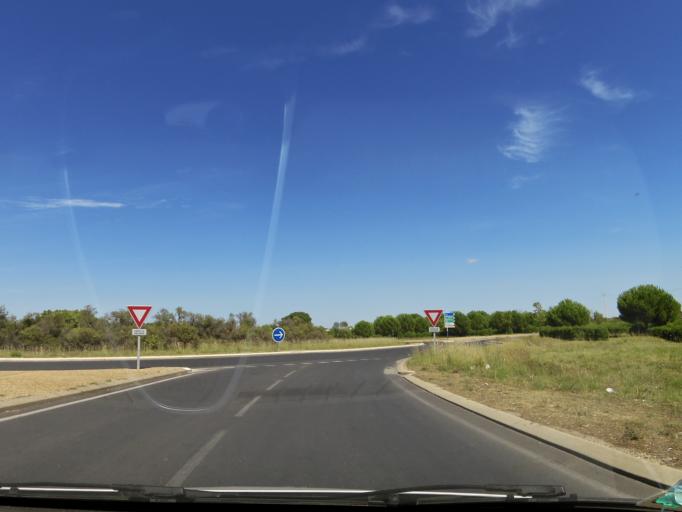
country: FR
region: Languedoc-Roussillon
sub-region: Departement de l'Herault
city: Vendargues
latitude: 43.6676
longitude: 3.9745
